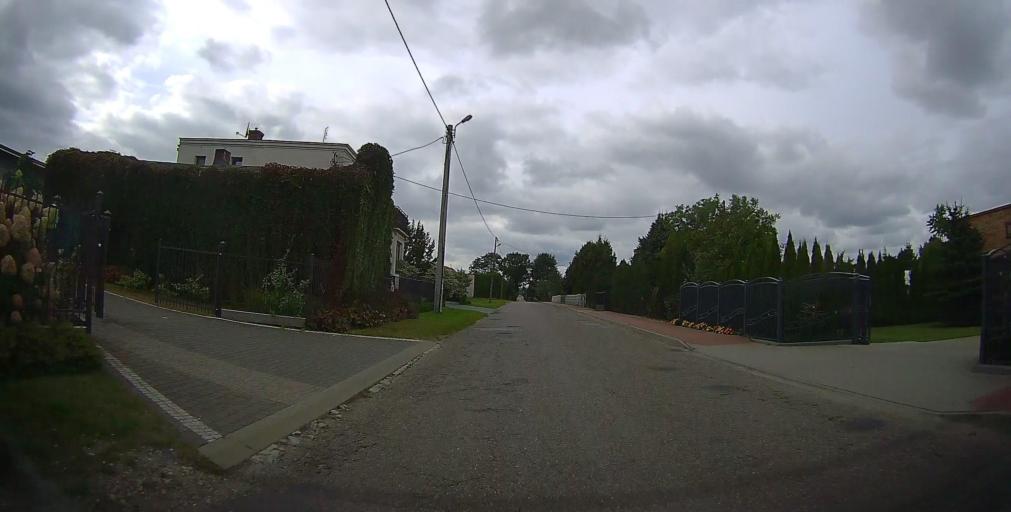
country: PL
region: Masovian Voivodeship
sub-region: Powiat grojecki
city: Belsk Duzy
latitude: 51.8193
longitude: 20.8214
